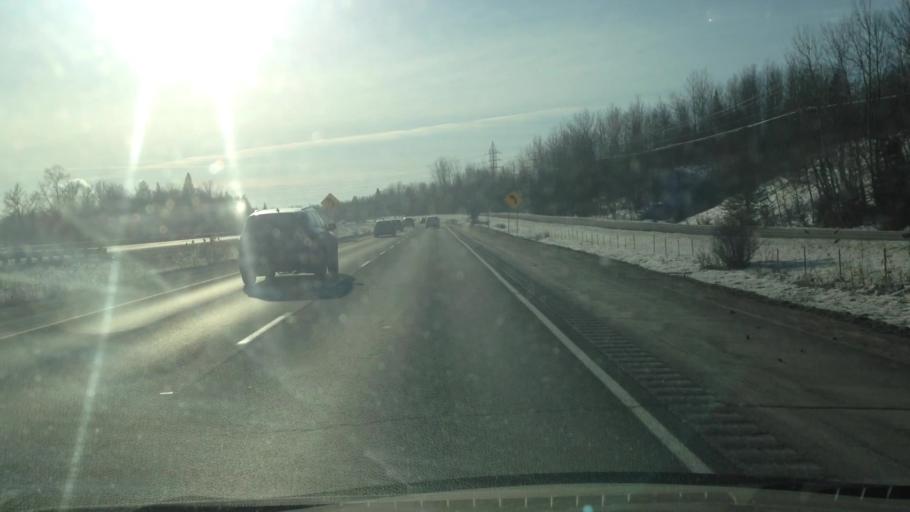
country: CA
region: Quebec
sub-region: Laurentides
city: Prevost
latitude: 45.8261
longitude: -74.0579
